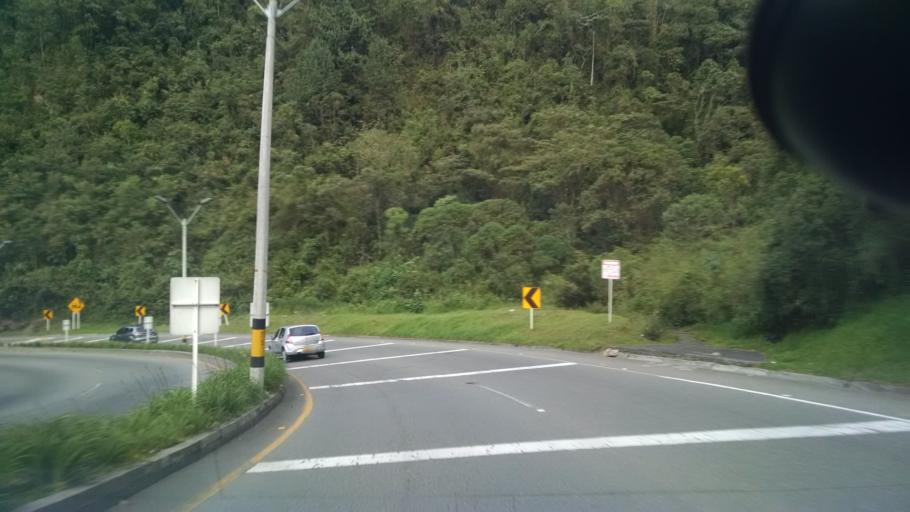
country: CO
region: Antioquia
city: Envigado
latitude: 6.1600
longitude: -75.5457
